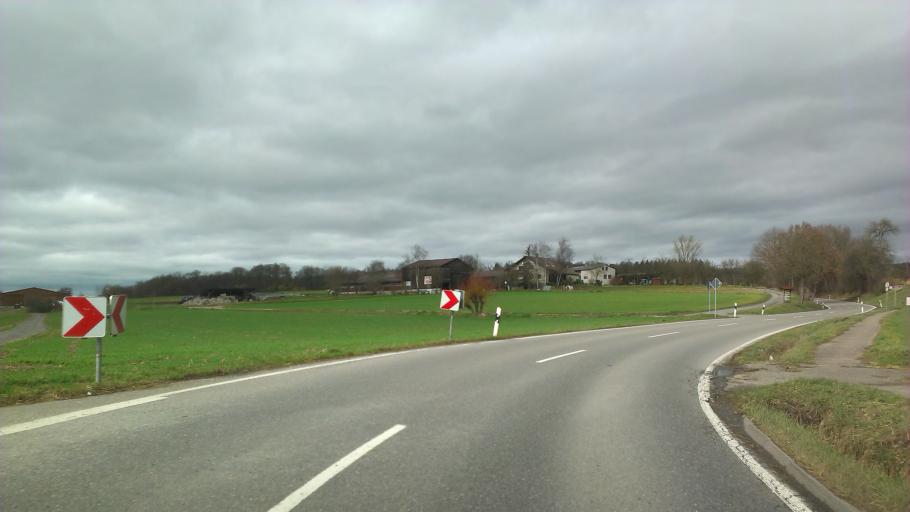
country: DE
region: Baden-Wuerttemberg
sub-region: Karlsruhe Region
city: Illingen
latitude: 48.9614
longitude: 8.9094
